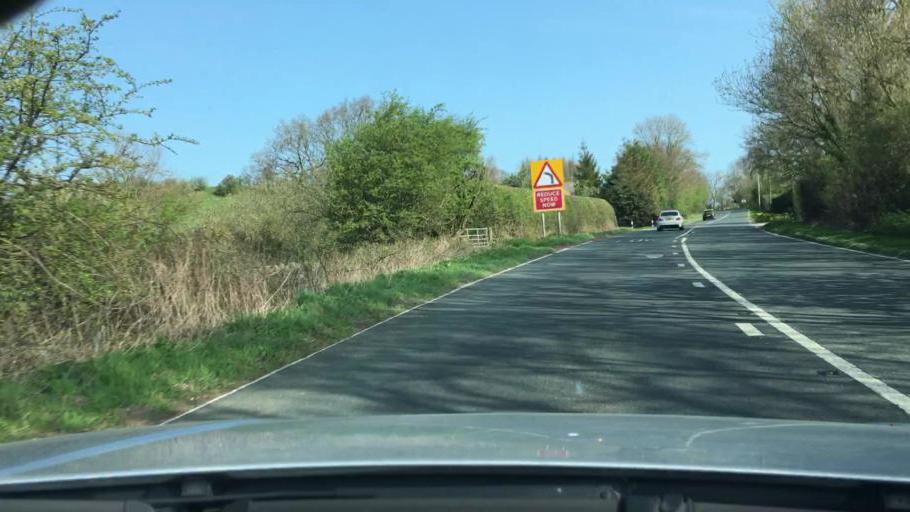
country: GB
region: England
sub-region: North Yorkshire
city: Pannal
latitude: 53.9369
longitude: -1.5368
